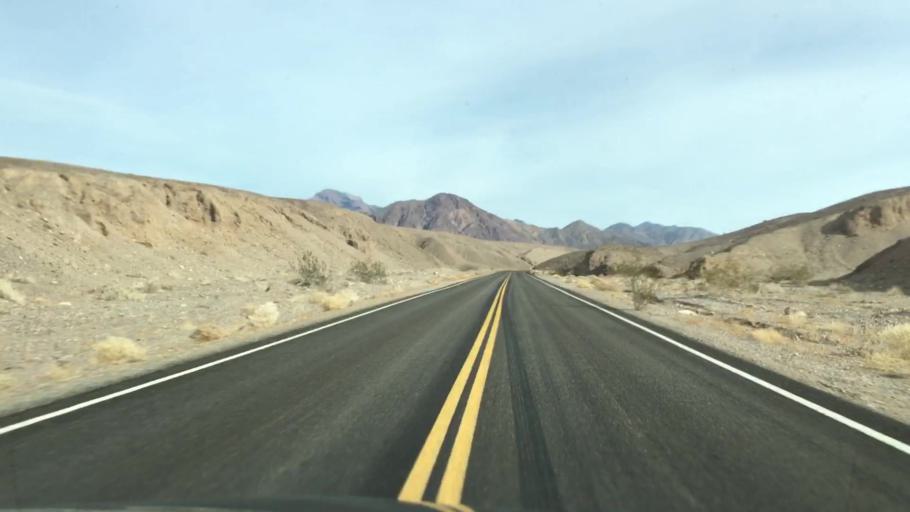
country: US
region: Nevada
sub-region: Nye County
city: Beatty
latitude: 36.6626
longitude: -117.0190
